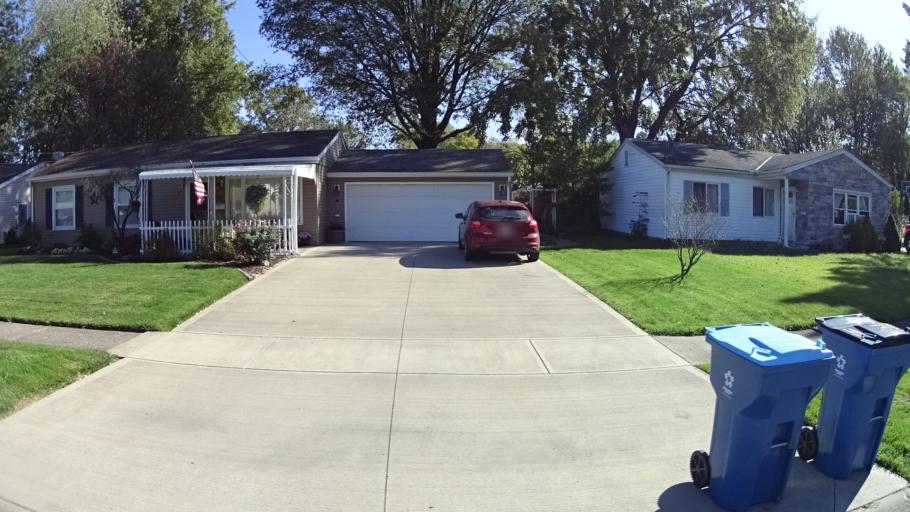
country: US
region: Ohio
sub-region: Lorain County
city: Lorain
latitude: 41.4157
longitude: -82.1715
